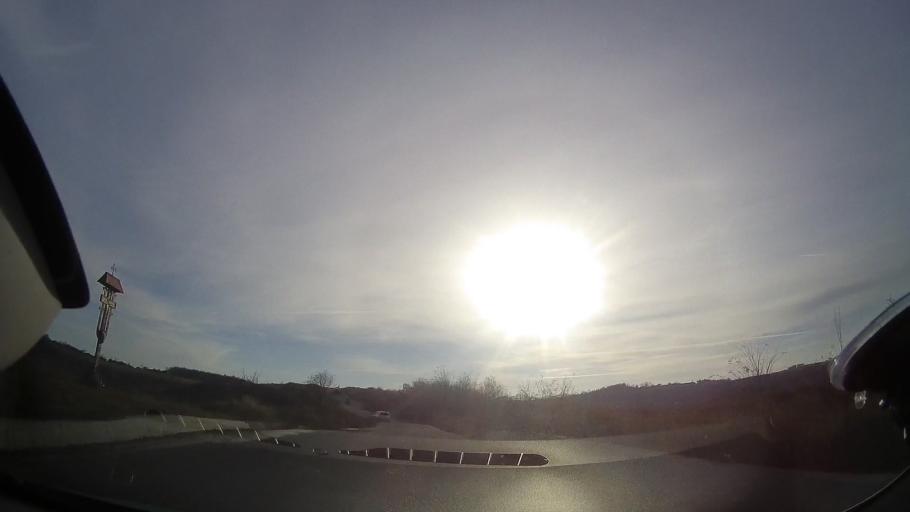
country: RO
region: Bihor
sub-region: Comuna Sarbi
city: Burzuc
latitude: 47.1304
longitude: 22.1870
